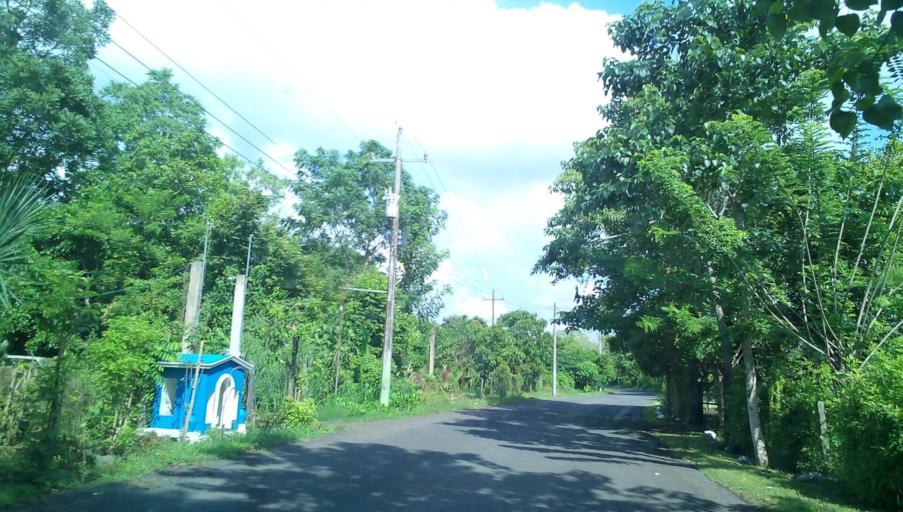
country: MX
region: Veracruz
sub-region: Citlaltepetl
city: Las Sabinas
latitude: 21.3512
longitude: -97.8958
